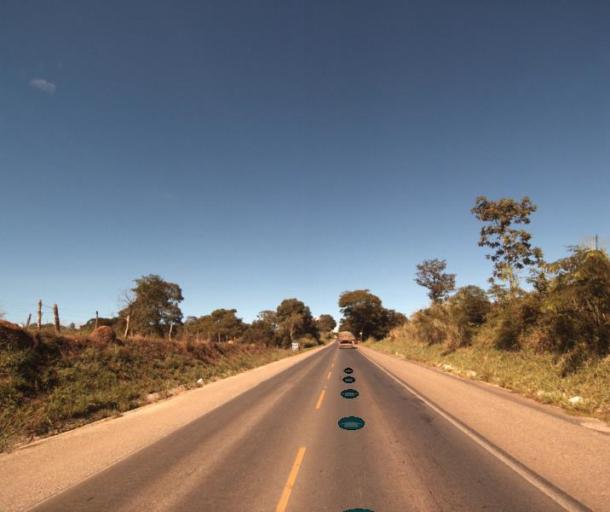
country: BR
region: Goias
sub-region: Itapaci
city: Itapaci
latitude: -15.0336
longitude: -49.4346
